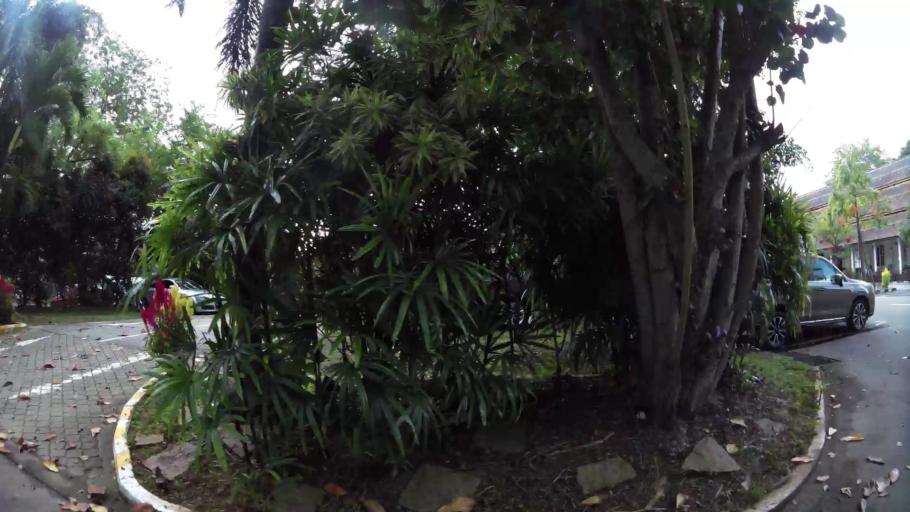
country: SG
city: Singapore
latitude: 1.3046
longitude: 103.8097
